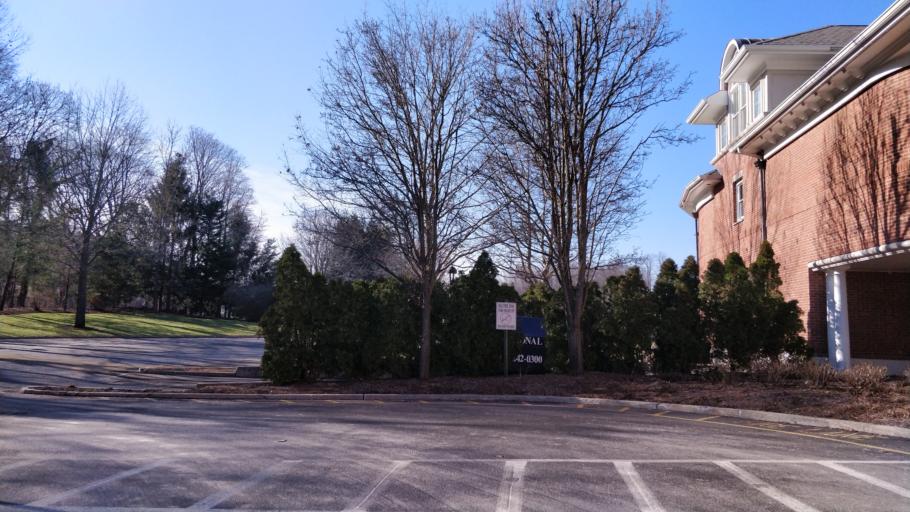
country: US
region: New York
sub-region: Nassau County
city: Locust Valley
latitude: 40.8642
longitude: -73.5954
